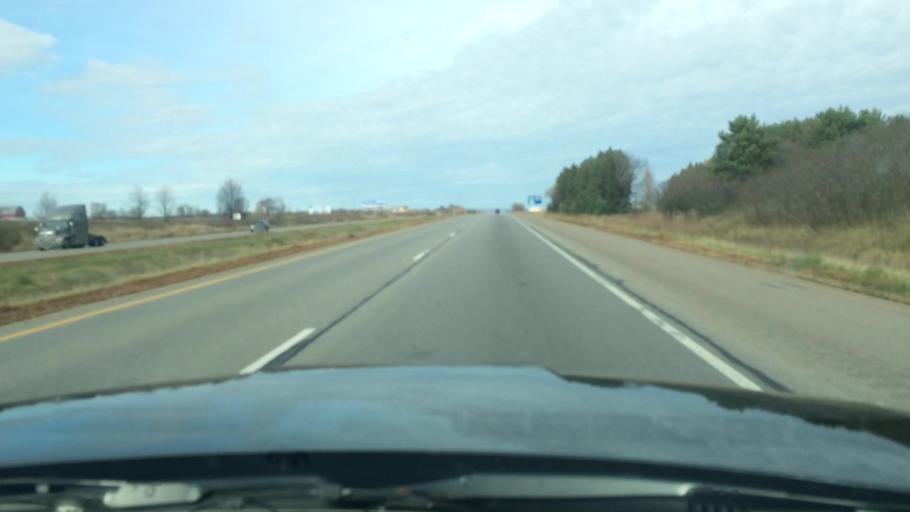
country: US
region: Wisconsin
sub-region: Marathon County
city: Mosinee
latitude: 44.7679
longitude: -89.6799
